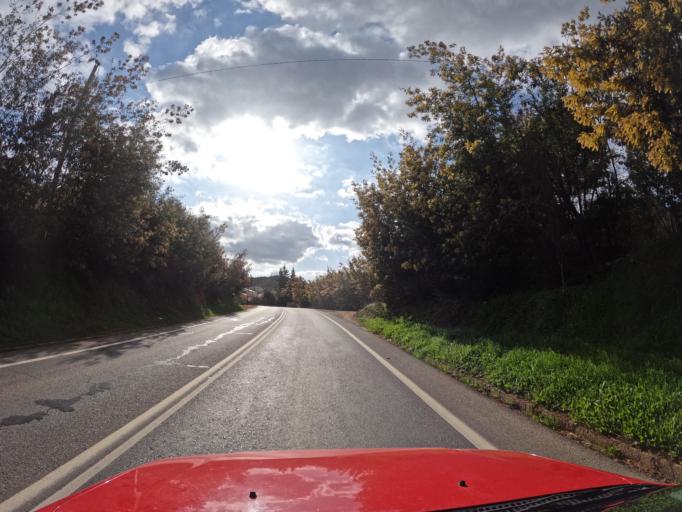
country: CL
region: Maule
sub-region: Provincia de Talca
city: Constitucion
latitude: -35.5496
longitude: -72.1465
